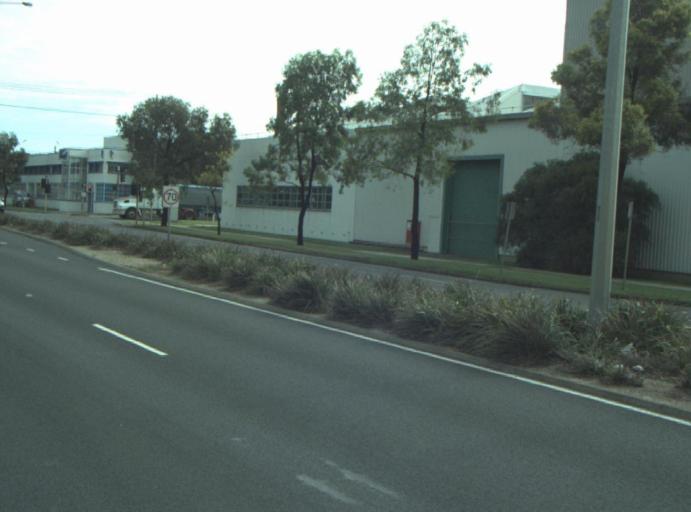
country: AU
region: Victoria
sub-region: Greater Geelong
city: Bell Park
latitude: -38.1158
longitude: 144.3543
